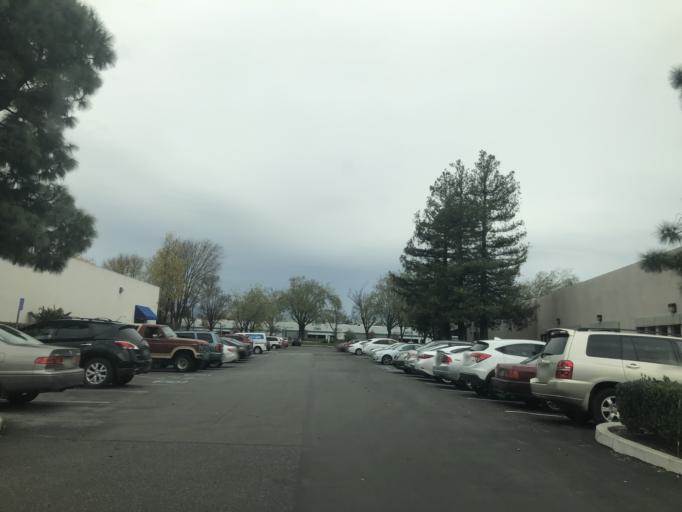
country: US
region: California
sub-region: Santa Clara County
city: San Jose
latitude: 37.3785
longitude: -121.9163
